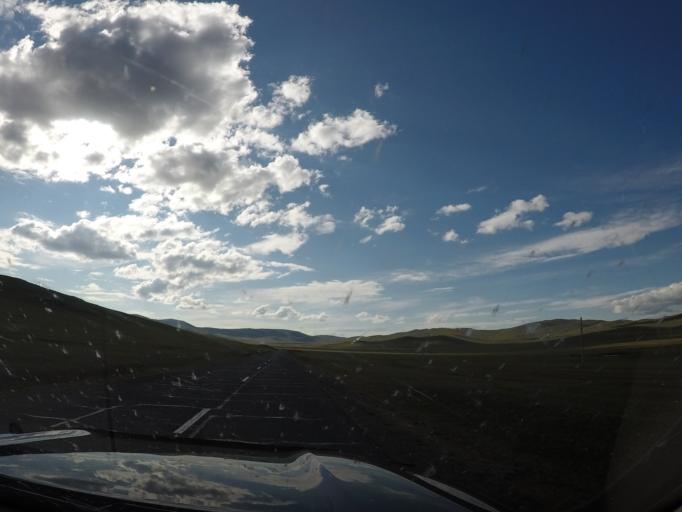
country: MN
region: Hentiy
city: Modot
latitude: 47.7606
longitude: 108.9272
